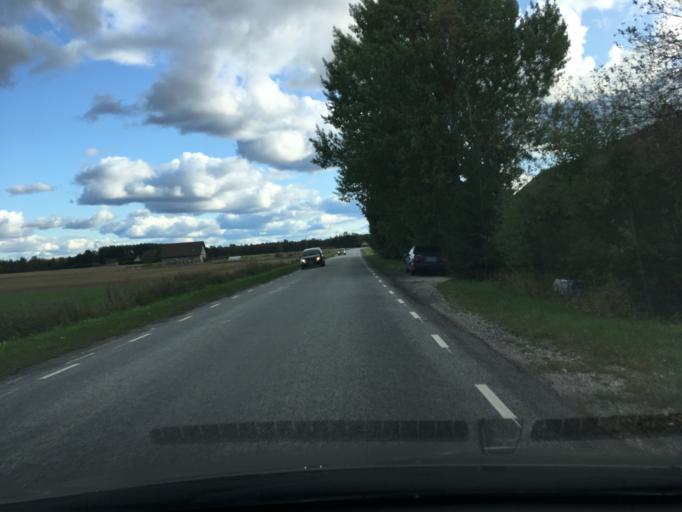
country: EE
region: Harju
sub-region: Raasiku vald
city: Raasiku
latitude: 59.3306
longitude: 25.1578
